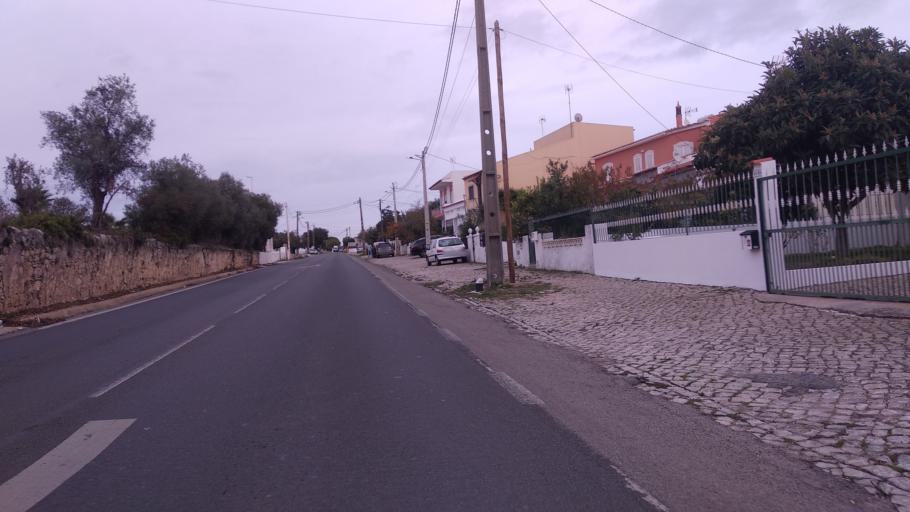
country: PT
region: Faro
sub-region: Loule
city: Loule
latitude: 37.1396
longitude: -7.9864
